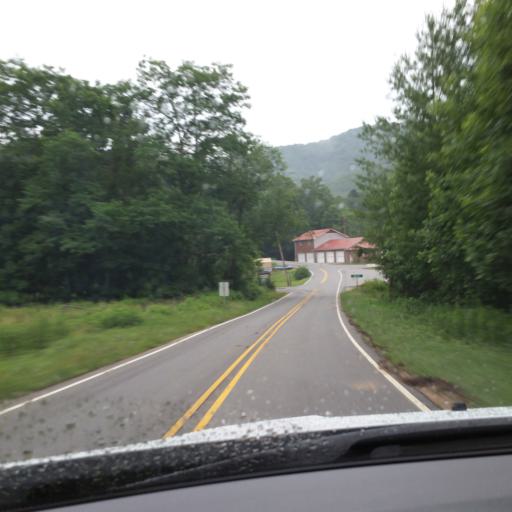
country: US
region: North Carolina
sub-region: Yancey County
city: Burnsville
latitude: 35.7704
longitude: -82.1858
